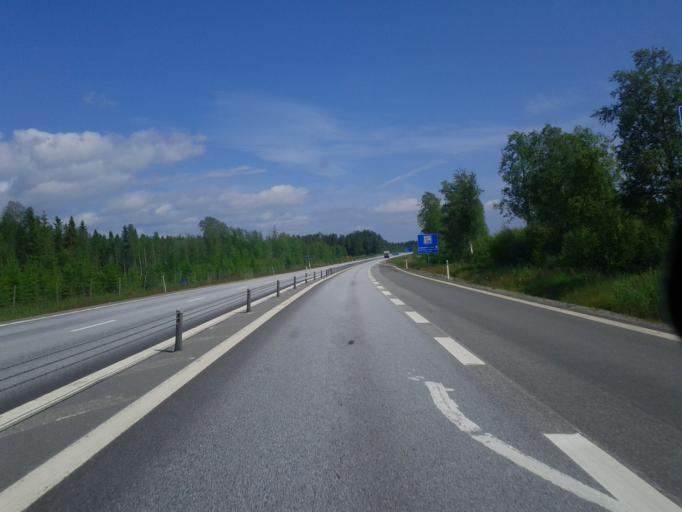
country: SE
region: Vaesterbotten
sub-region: Nordmalings Kommun
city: Nordmaling
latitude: 63.5737
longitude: 19.4445
